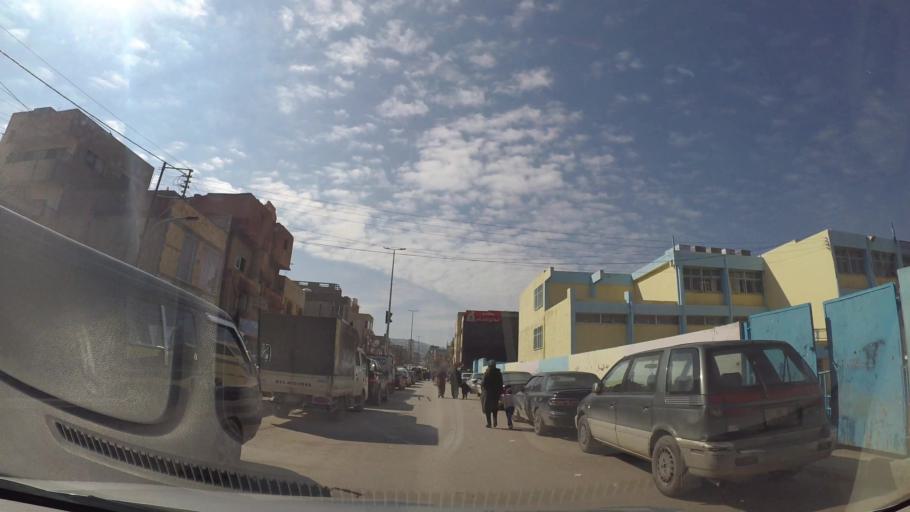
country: JO
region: Amman
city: Al Jubayhah
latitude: 32.0763
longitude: 35.8454
